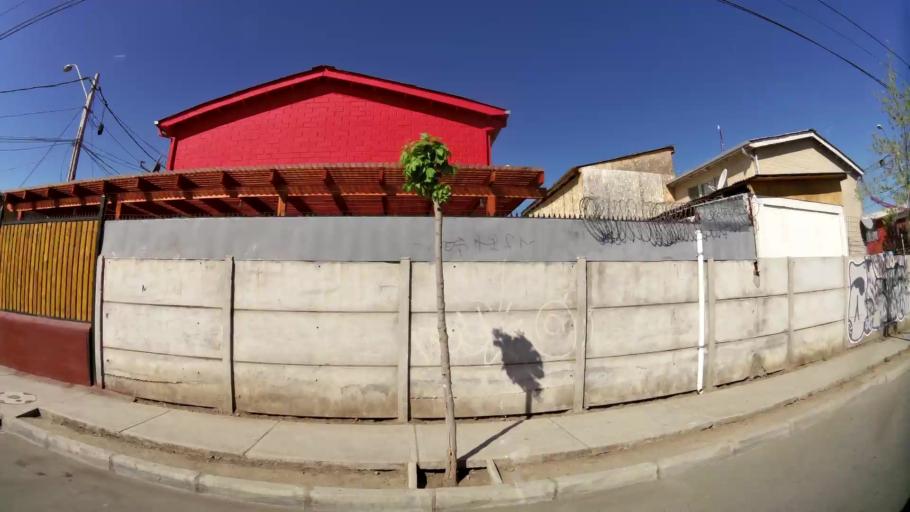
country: CL
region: Santiago Metropolitan
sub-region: Provincia de Santiago
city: La Pintana
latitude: -33.6207
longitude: -70.6255
